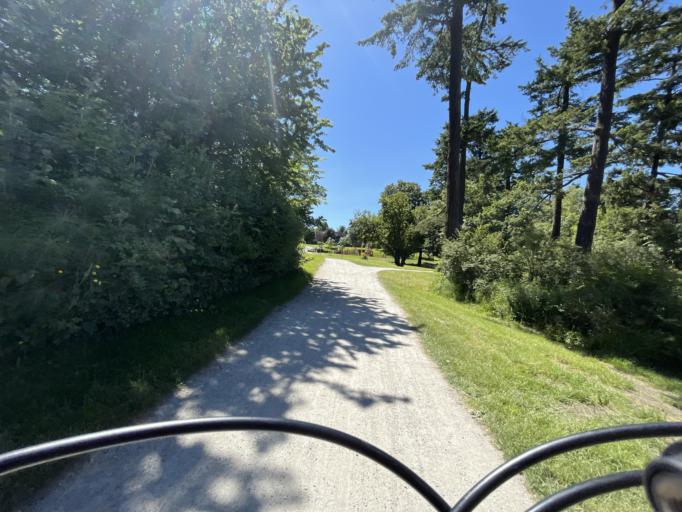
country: CA
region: British Columbia
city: Victoria
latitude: 48.4377
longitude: -123.3863
